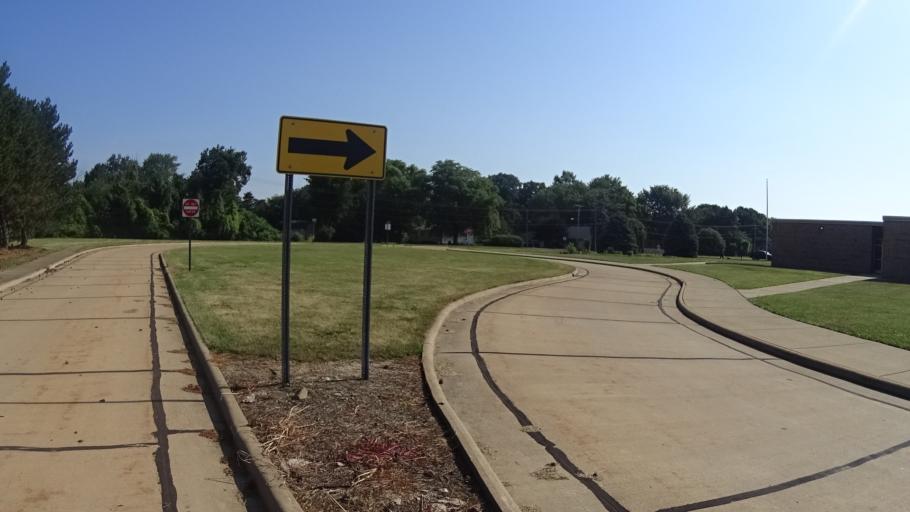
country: US
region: Ohio
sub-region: Erie County
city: Huron
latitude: 41.4059
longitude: -82.5872
